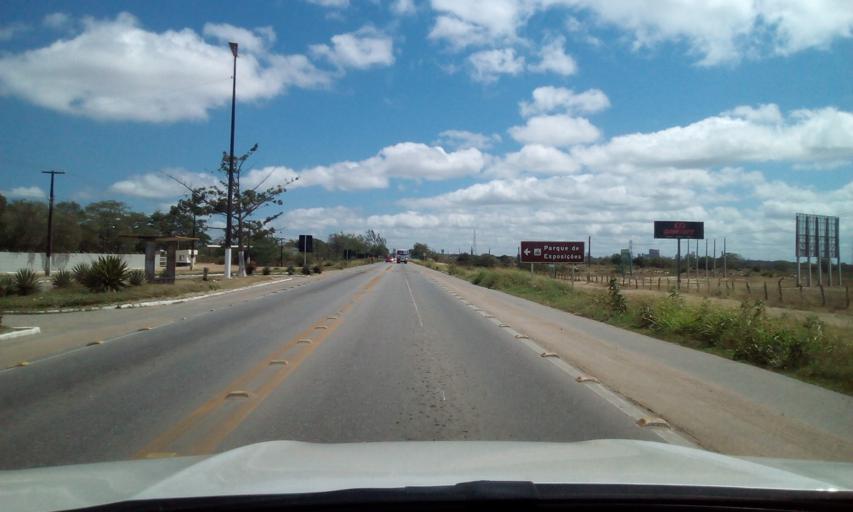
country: BR
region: Paraiba
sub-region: Campina Grande
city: Campina Grande
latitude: -7.2859
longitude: -35.8896
